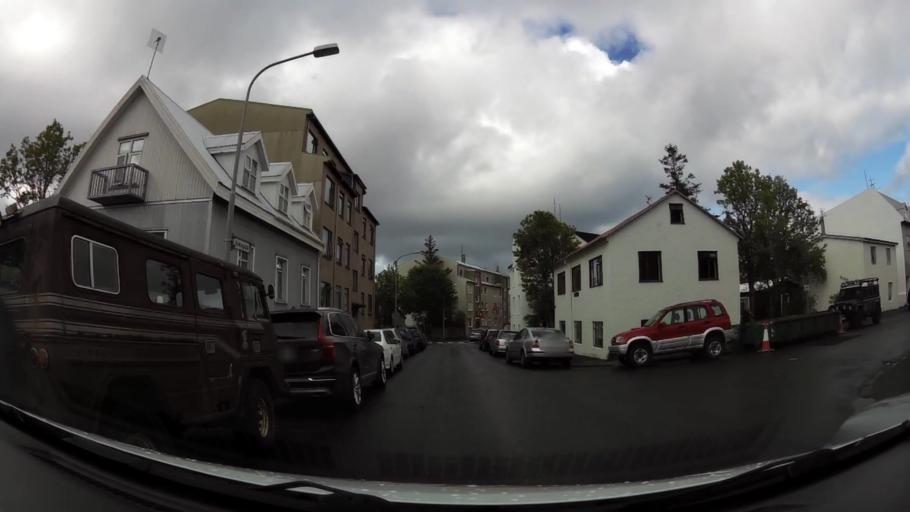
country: IS
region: Capital Region
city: Seltjarnarnes
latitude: 64.1492
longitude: -21.9545
